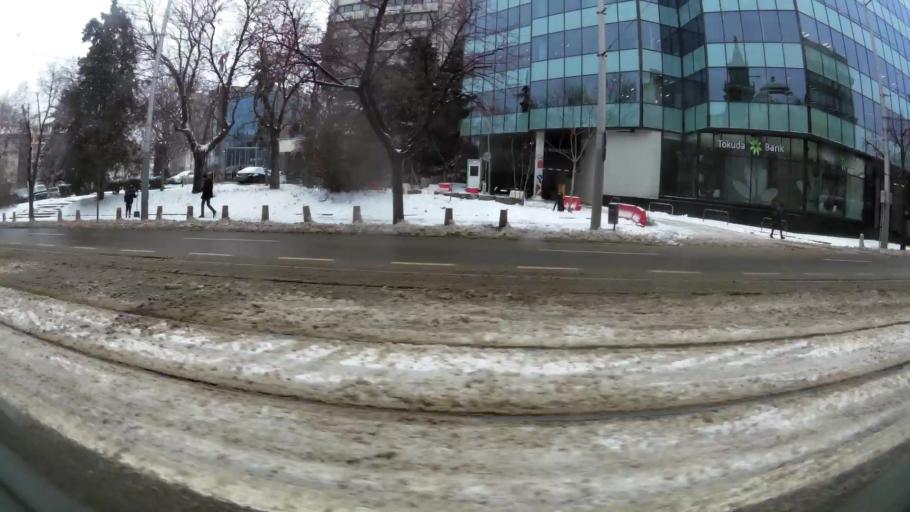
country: BG
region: Sofia-Capital
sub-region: Stolichna Obshtina
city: Sofia
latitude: 42.6955
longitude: 23.3153
